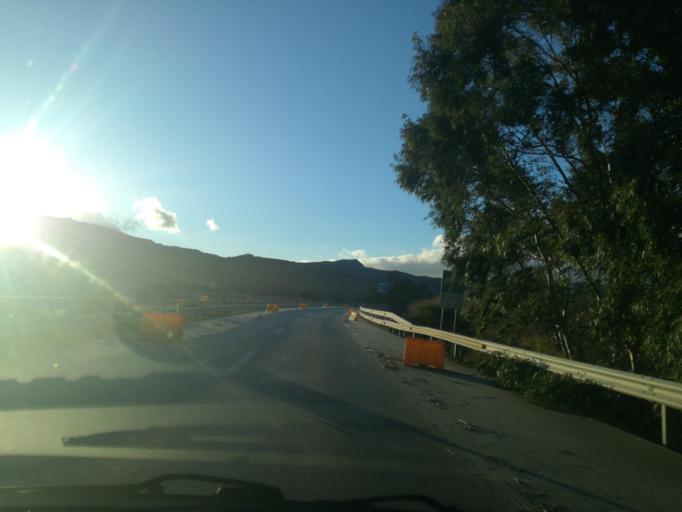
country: IT
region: Sicily
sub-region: Palermo
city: Polizzi Generosa
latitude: 37.7436
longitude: 13.9813
